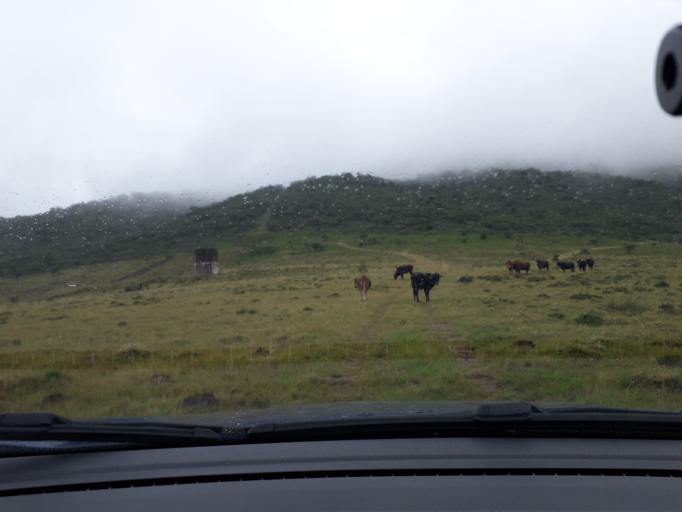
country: ZA
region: Eastern Cape
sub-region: Buffalo City Metropolitan Municipality
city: Bhisho
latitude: -32.7307
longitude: 27.3708
